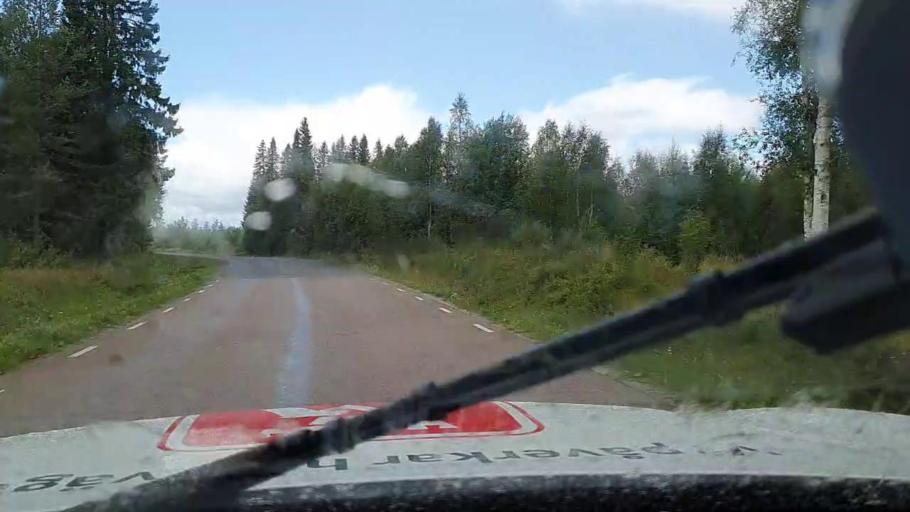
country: SE
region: Jaemtland
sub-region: Stroemsunds Kommun
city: Stroemsund
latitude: 63.8782
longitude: 15.3553
